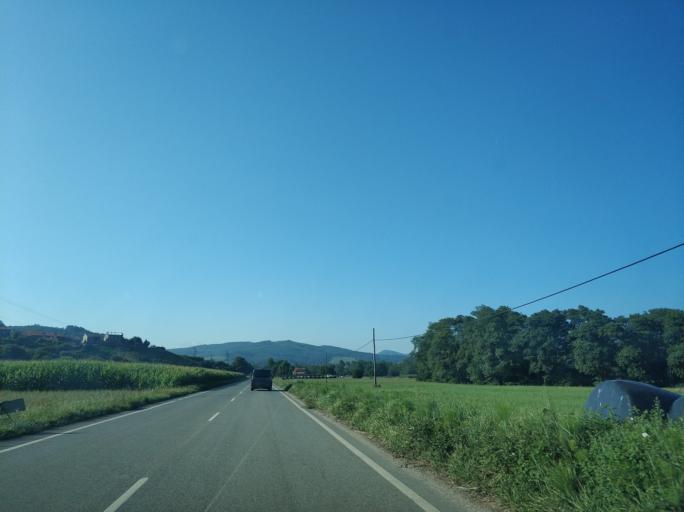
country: ES
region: Cantabria
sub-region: Provincia de Cantabria
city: Polanco
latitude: 43.3771
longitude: -3.9640
